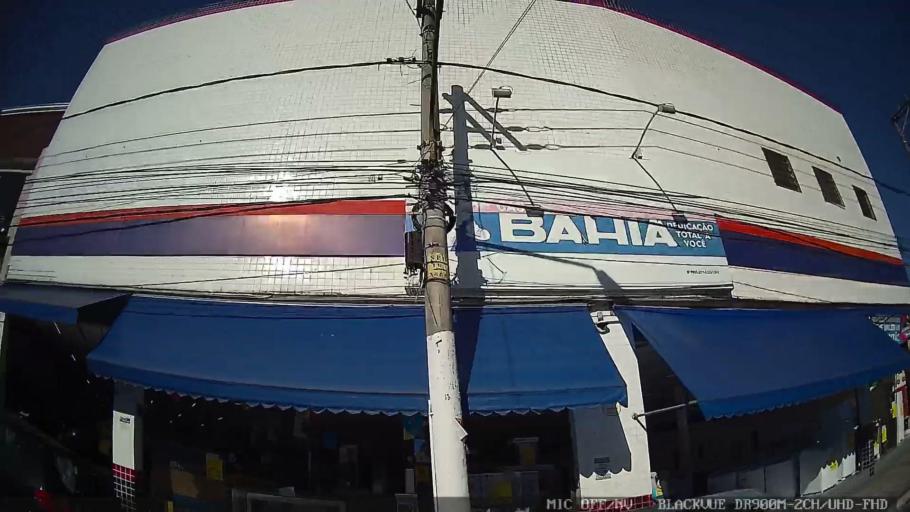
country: BR
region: Sao Paulo
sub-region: Guarulhos
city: Guarulhos
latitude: -23.5451
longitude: -46.5155
